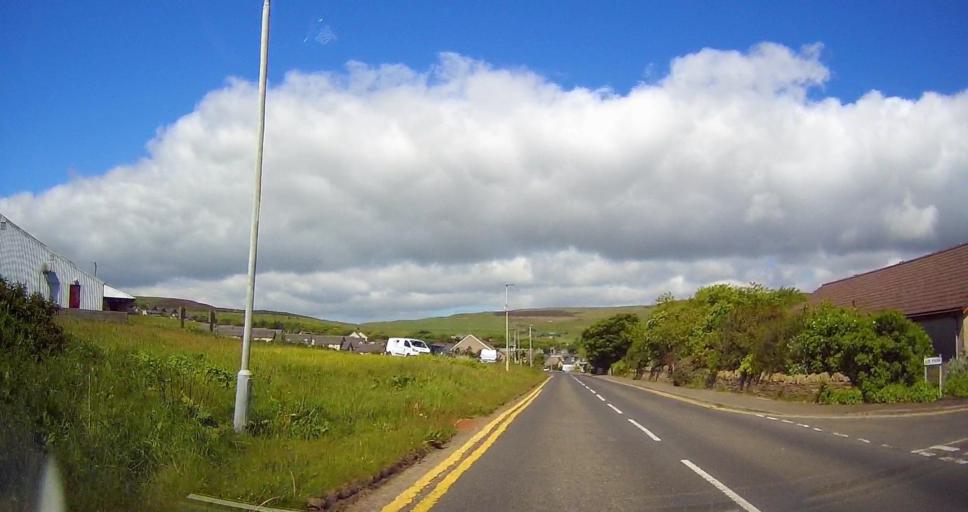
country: GB
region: Scotland
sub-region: Orkney Islands
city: Orkney
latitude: 59.0022
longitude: -3.1062
